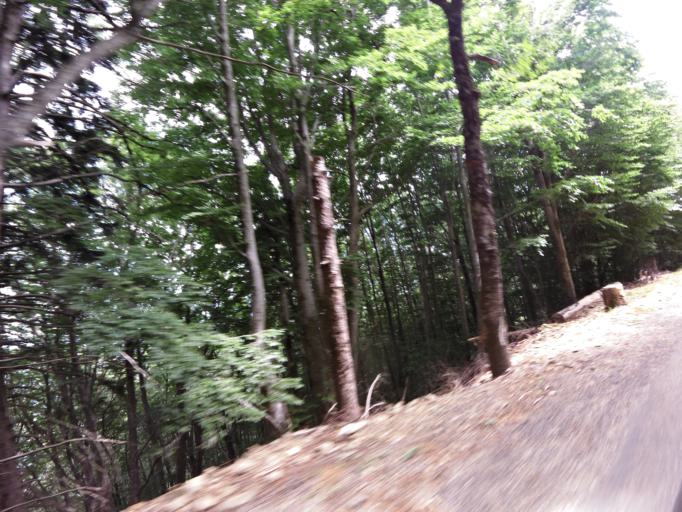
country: FR
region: Languedoc-Roussillon
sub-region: Departement du Gard
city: Valleraugue
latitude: 44.0544
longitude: 3.6065
